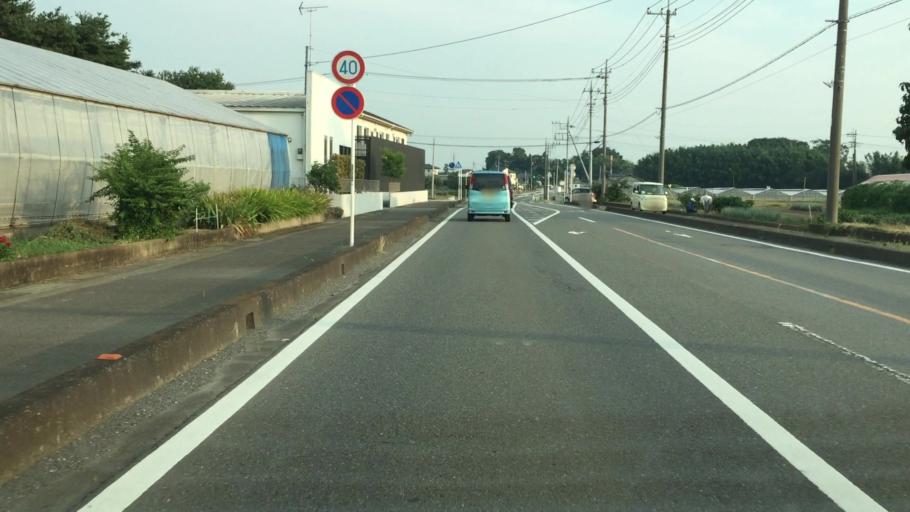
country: JP
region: Gunma
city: Tatebayashi
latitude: 36.2309
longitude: 139.5897
